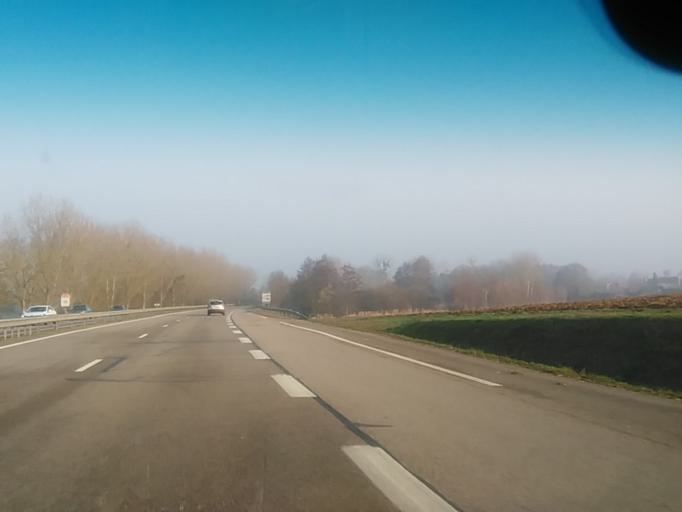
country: FR
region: Lower Normandy
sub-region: Departement du Calvados
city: Potigny
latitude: 48.9516
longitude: -0.2223
